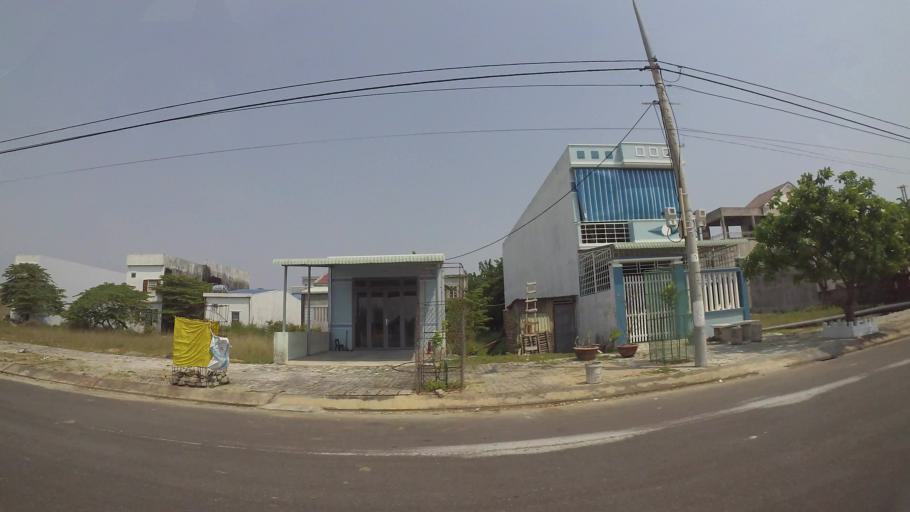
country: VN
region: Da Nang
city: Cam Le
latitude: 15.9754
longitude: 108.2118
